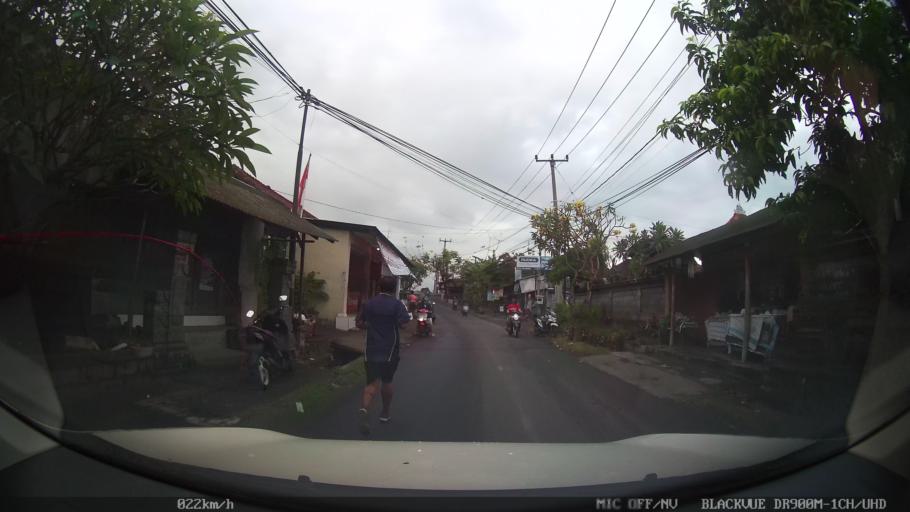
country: ID
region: Bali
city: Banjar Pasekan
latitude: -8.6163
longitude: 115.2758
